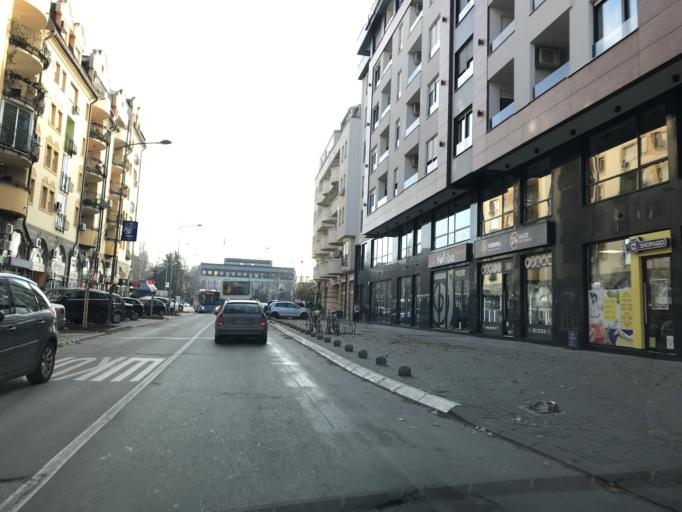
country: RS
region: Autonomna Pokrajina Vojvodina
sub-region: Juznobacki Okrug
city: Novi Sad
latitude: 45.2488
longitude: 19.8486
